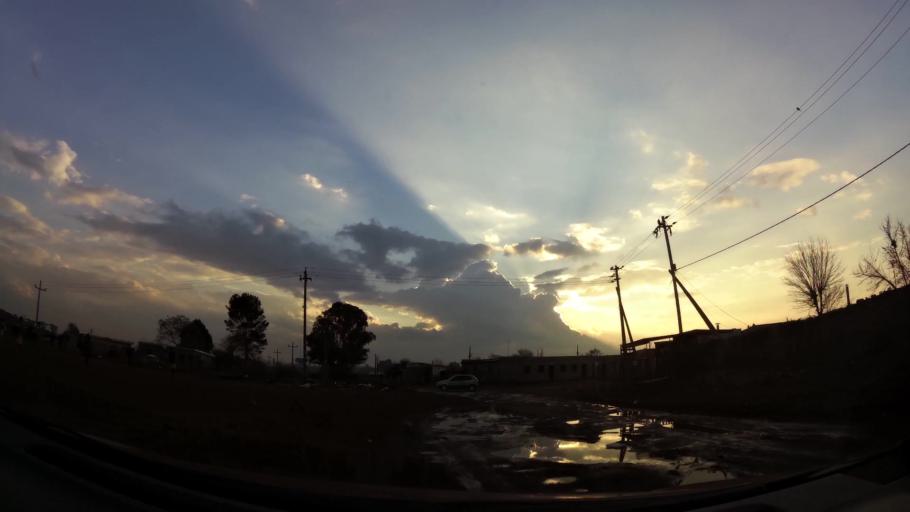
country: ZA
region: Gauteng
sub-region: City of Johannesburg Metropolitan Municipality
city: Orange Farm
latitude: -26.5393
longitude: 27.8454
